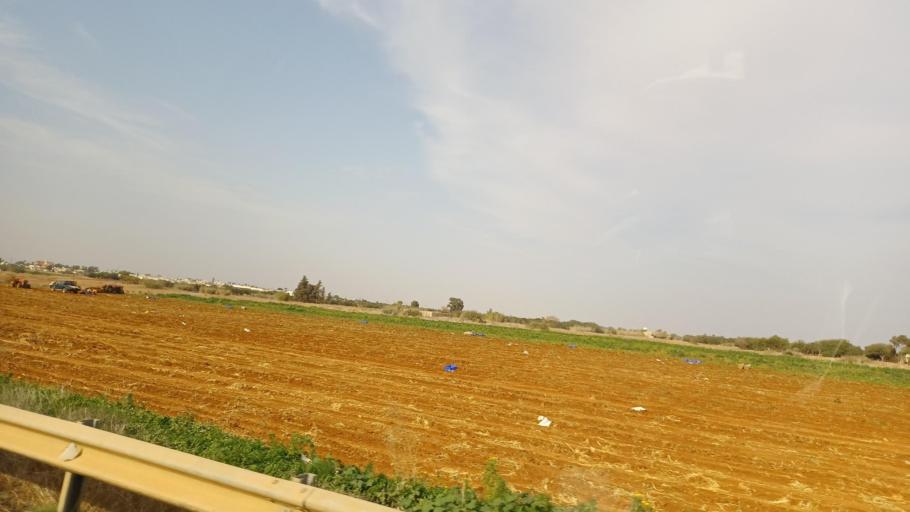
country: CY
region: Ammochostos
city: Frenaros
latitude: 35.0625
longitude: 33.8914
